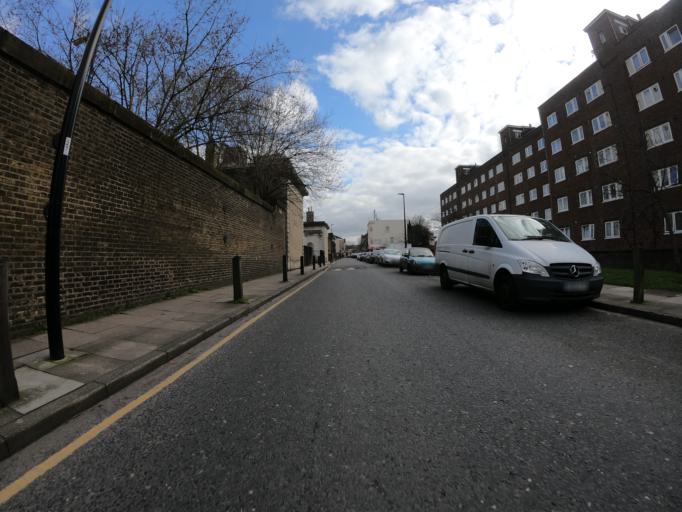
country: GB
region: England
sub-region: Greater London
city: Woolwich
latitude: 51.4887
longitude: 0.0548
